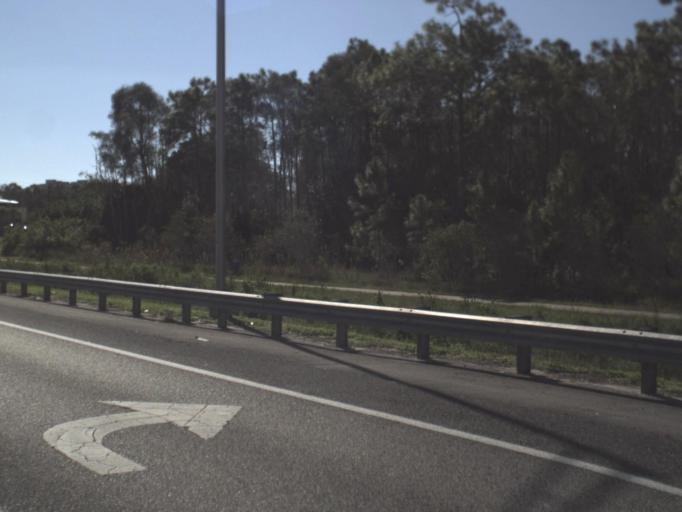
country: US
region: Florida
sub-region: Lee County
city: Fort Myers
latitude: 26.6381
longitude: -81.8128
